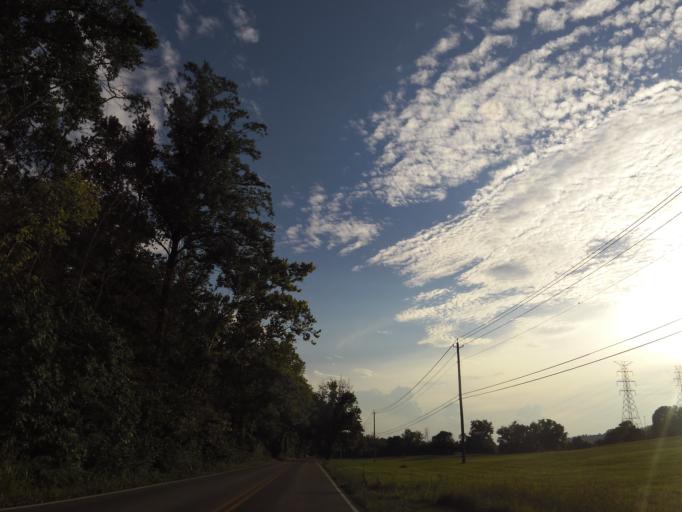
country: US
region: Tennessee
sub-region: Knox County
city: Knoxville
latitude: 36.0351
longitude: -83.9666
